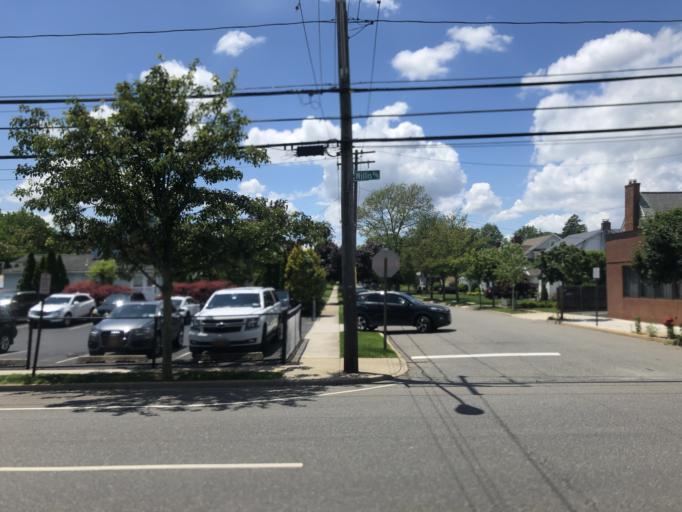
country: US
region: New York
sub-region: Nassau County
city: Williston Park
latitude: 40.7531
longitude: -73.6433
